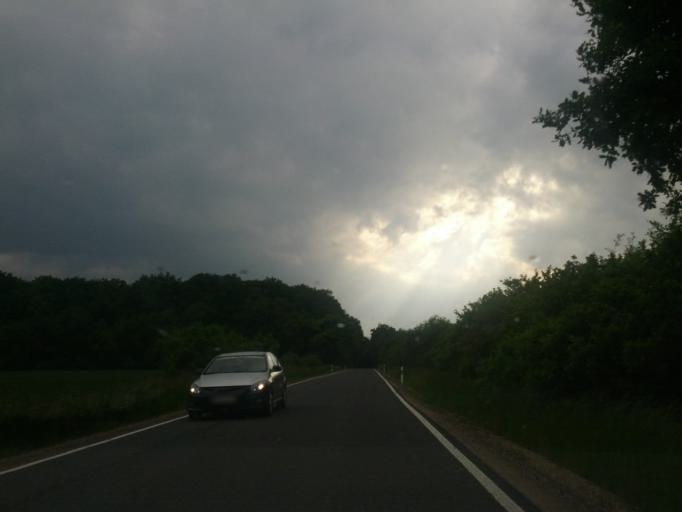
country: DE
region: Thuringia
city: Petriroda
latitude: 50.8793
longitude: 10.6701
